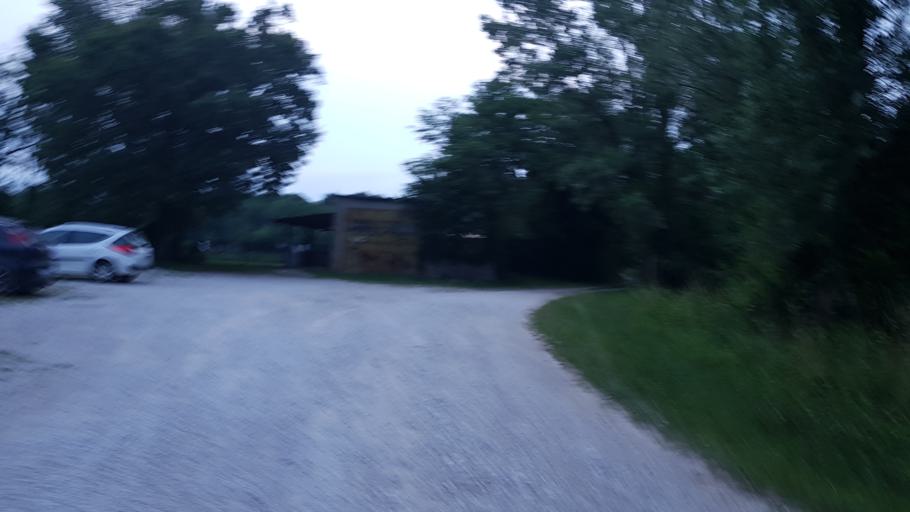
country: IT
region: Friuli Venezia Giulia
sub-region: Provincia di Gorizia
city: San Lorenzo Isontino
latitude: 45.9397
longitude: 13.5276
